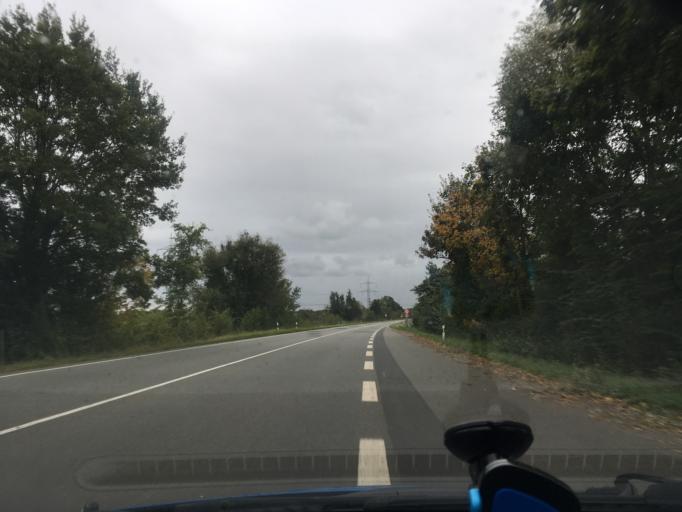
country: DE
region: Lower Saxony
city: Handorf
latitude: 53.3802
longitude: 10.3476
